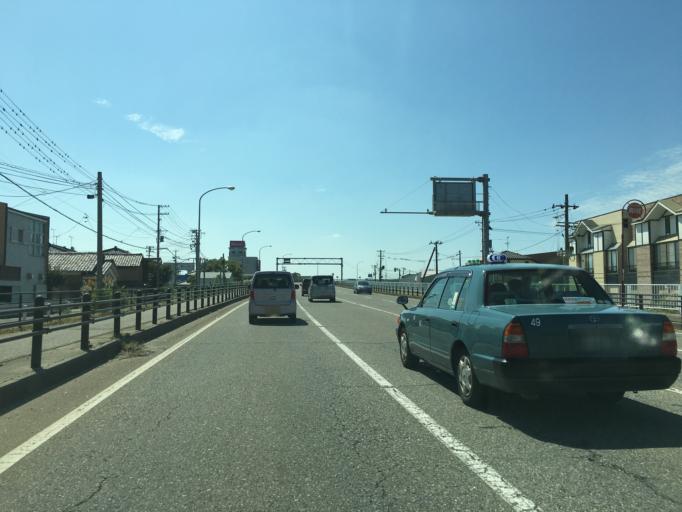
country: JP
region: Niigata
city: Niigata-shi
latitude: 37.9003
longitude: 139.0137
